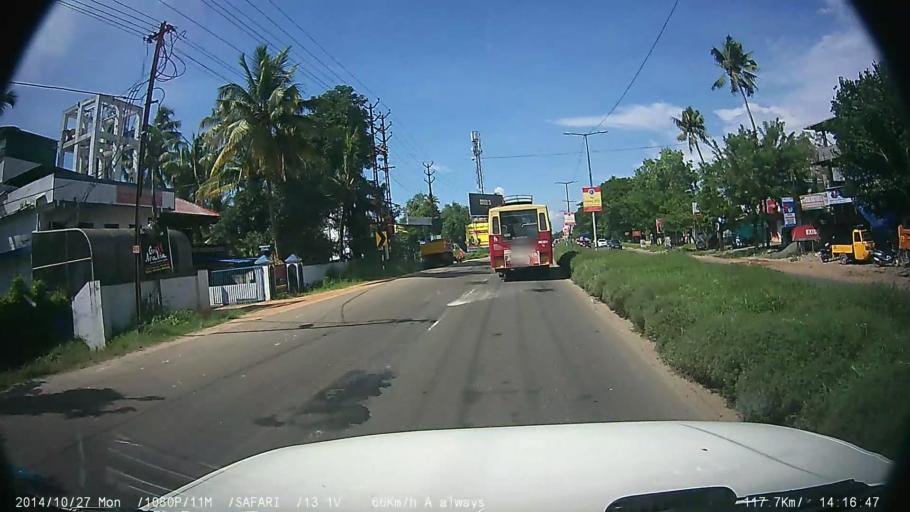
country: IN
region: Kerala
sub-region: Alappuzha
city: Arukutti
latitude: 9.8462
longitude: 76.3078
